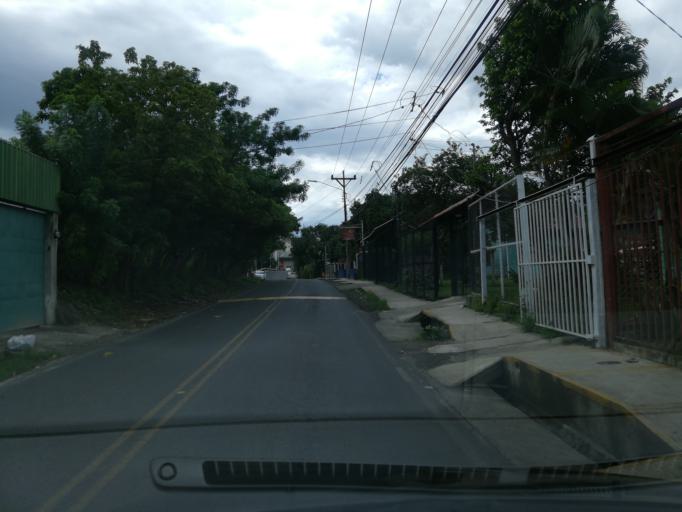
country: CR
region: Alajuela
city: Alajuela
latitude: 10.0027
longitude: -84.2106
